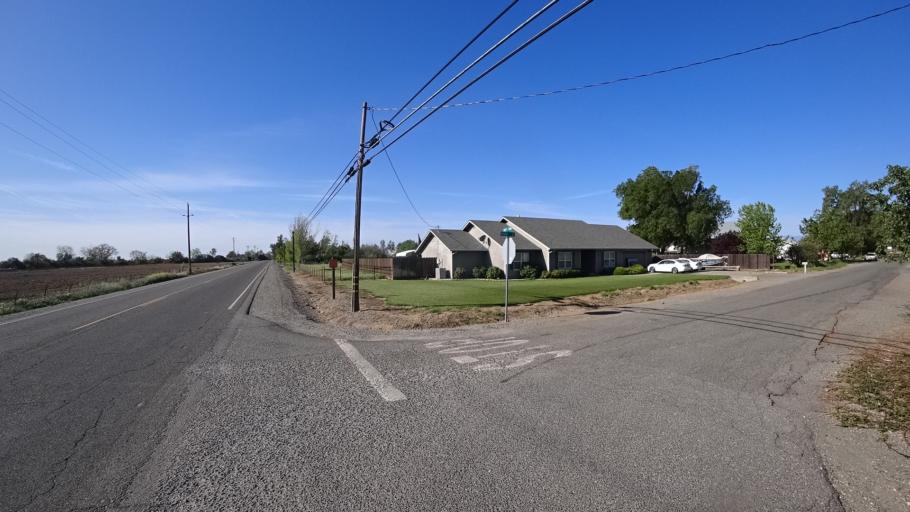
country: US
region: California
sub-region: Glenn County
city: Orland
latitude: 39.7220
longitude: -122.1971
